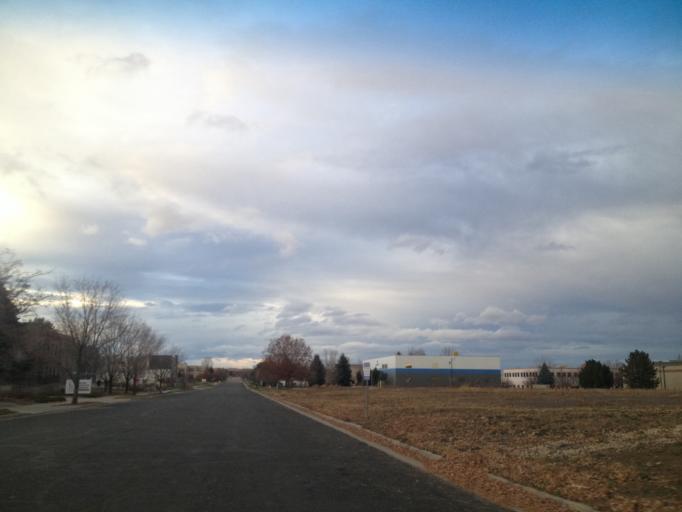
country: US
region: Colorado
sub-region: Boulder County
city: Louisville
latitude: 39.9610
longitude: -105.1197
